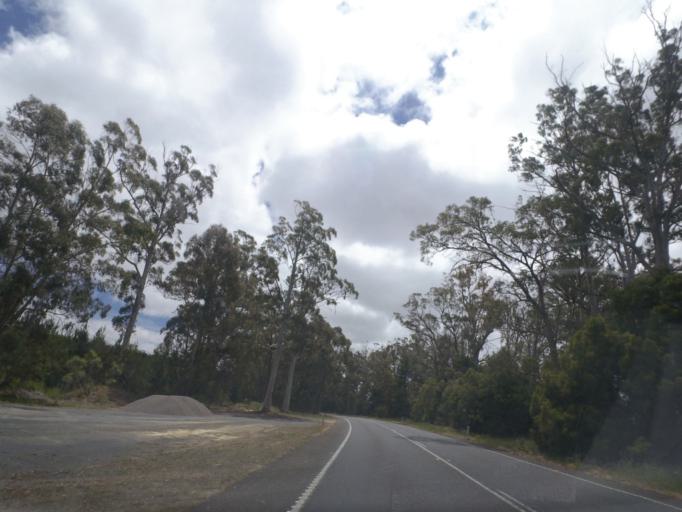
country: AU
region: Victoria
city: Brown Hill
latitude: -37.4857
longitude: 144.1536
